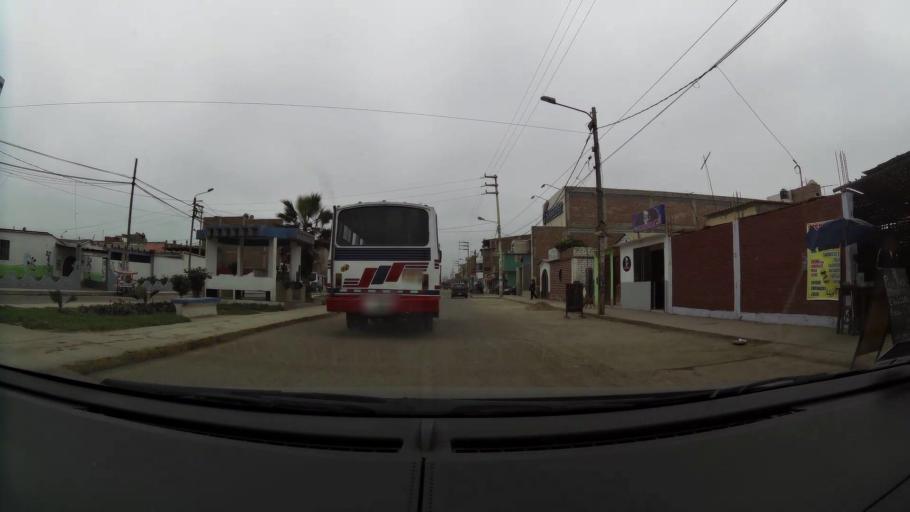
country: PE
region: La Libertad
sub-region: Provincia de Trujillo
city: Buenos Aires
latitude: -8.1434
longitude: -79.0550
